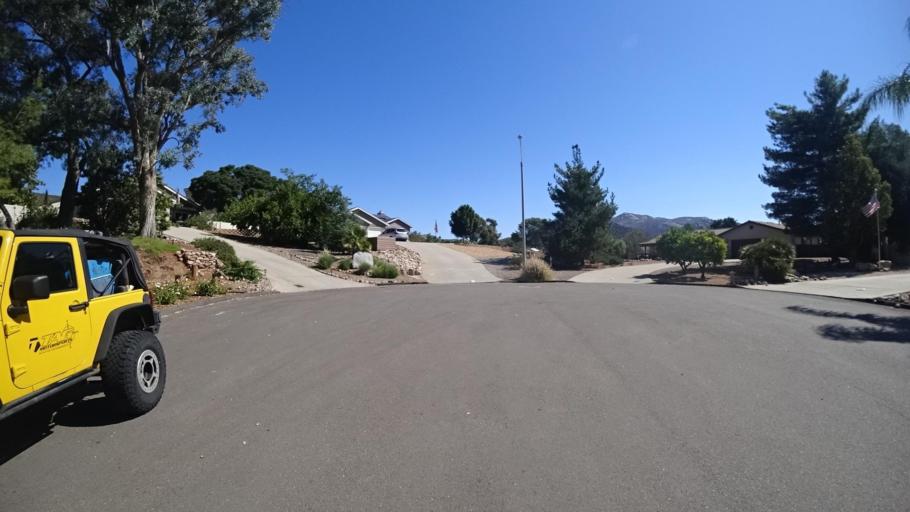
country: US
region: California
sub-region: San Diego County
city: San Diego Country Estates
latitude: 33.0195
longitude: -116.8110
